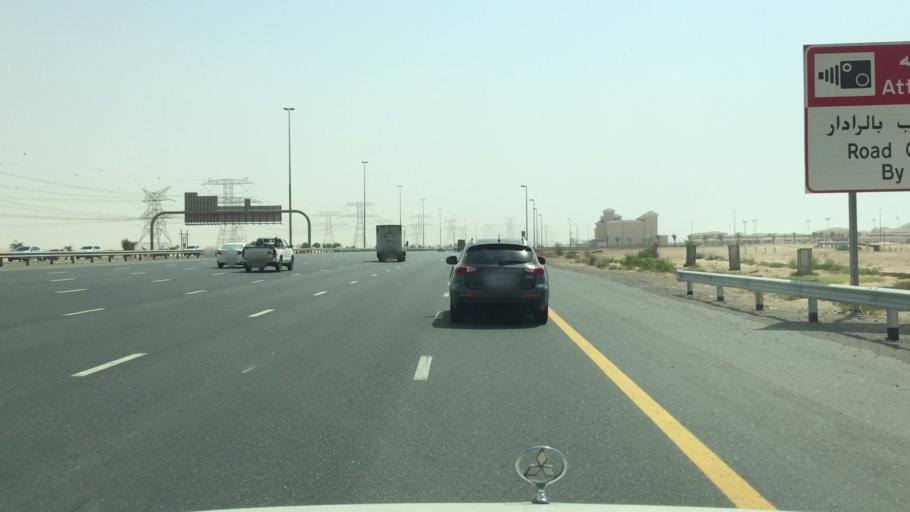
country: AE
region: Dubai
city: Dubai
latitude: 25.0776
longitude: 55.3771
